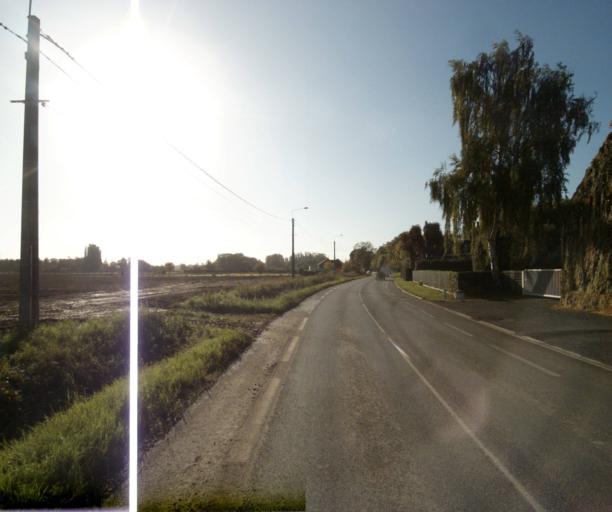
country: FR
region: Nord-Pas-de-Calais
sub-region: Departement du Nord
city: Verlinghem
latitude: 50.6749
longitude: 3.0016
